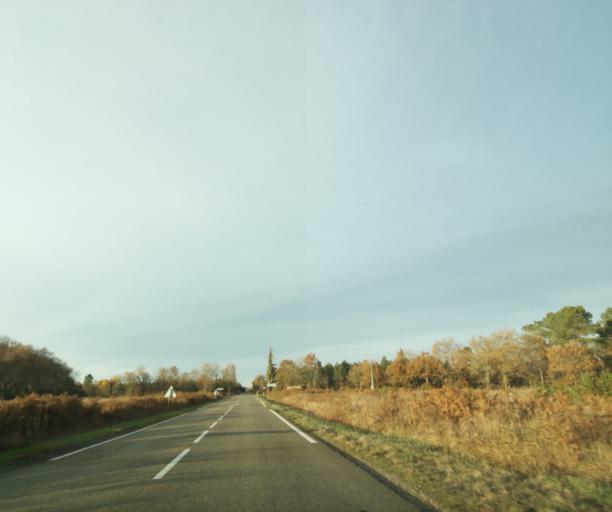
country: FR
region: Aquitaine
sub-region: Departement des Landes
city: Gabarret
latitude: 44.1132
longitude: -0.1027
